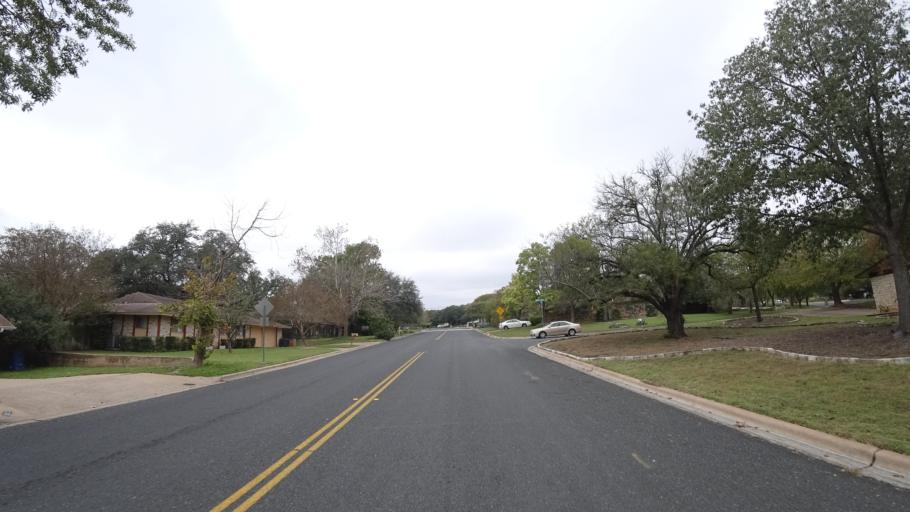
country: US
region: Texas
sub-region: Travis County
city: Barton Creek
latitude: 30.2370
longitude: -97.8801
